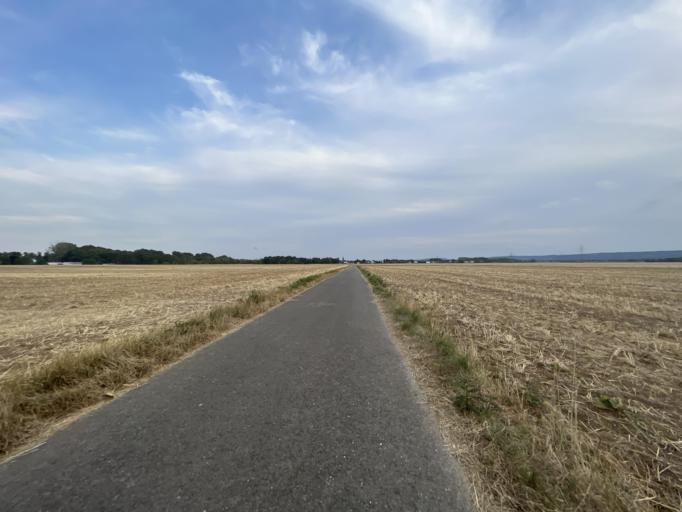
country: DE
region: North Rhine-Westphalia
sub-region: Regierungsbezirk Koln
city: Dueren
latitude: 50.8262
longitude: 6.4369
